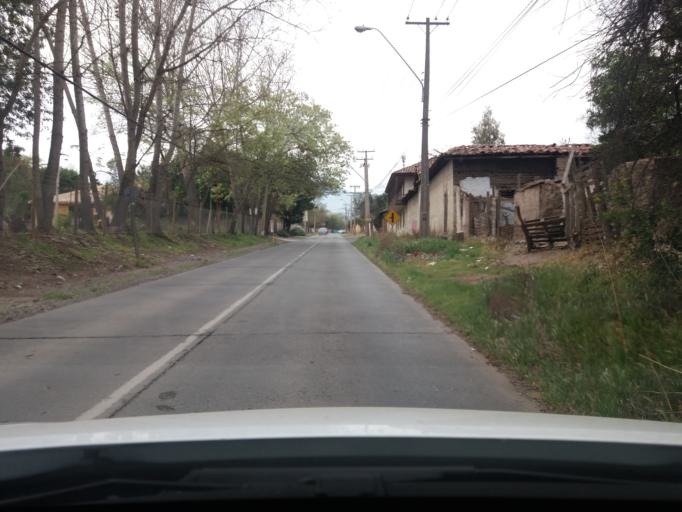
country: CL
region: Valparaiso
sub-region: Provincia de Los Andes
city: Los Andes
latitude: -32.8316
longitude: -70.6193
